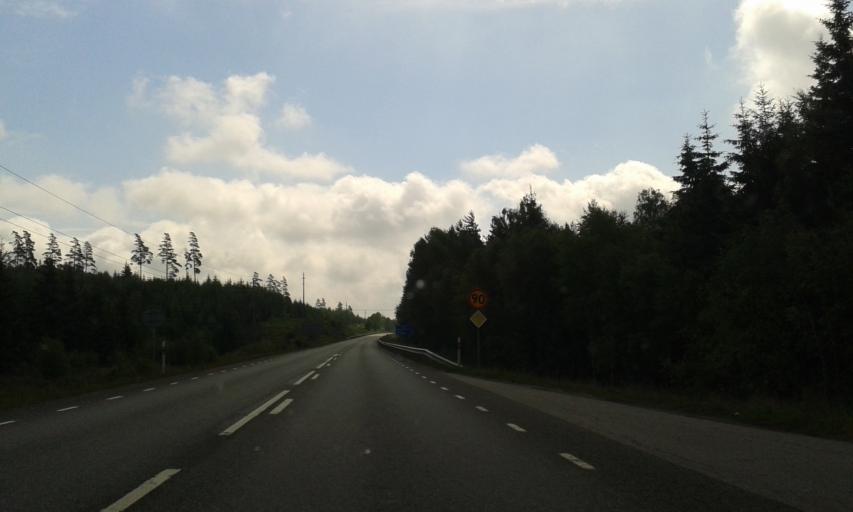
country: SE
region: Vaestra Goetaland
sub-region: Tranemo Kommun
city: Langhem
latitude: 57.6083
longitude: 13.1416
